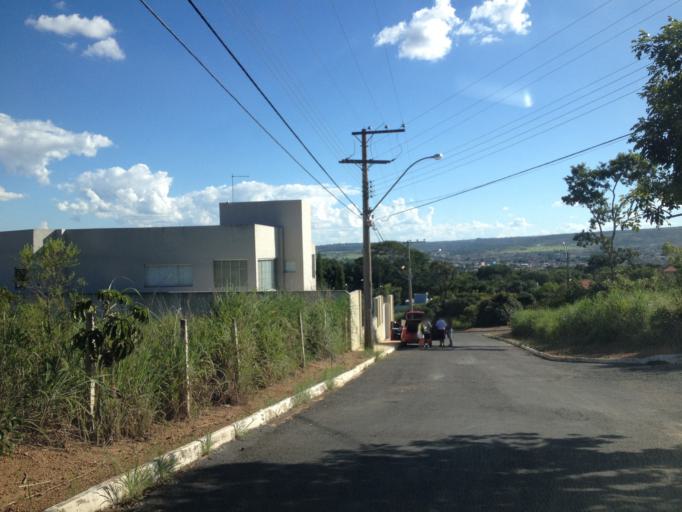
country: BR
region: Federal District
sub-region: Brasilia
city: Brasilia
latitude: -15.8888
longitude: -47.7573
